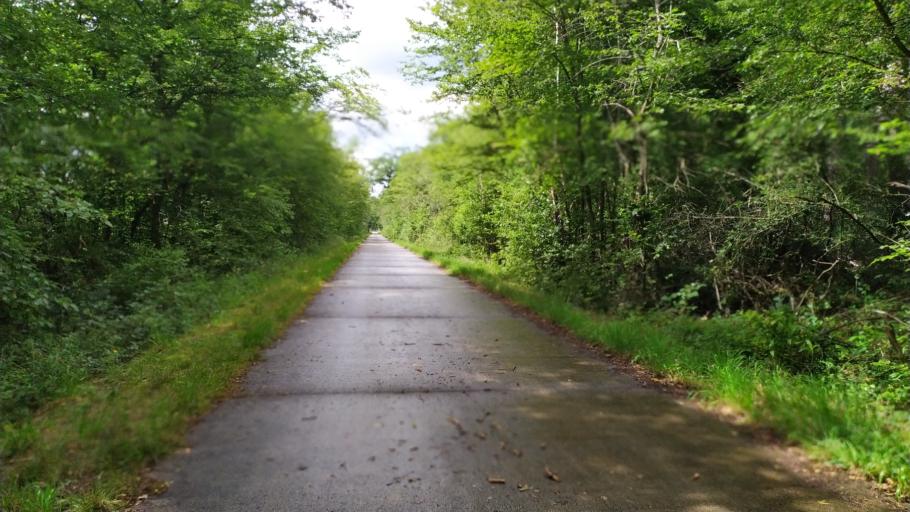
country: BE
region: Wallonia
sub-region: Province du Luxembourg
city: Wellin
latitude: 50.1508
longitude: 5.1364
